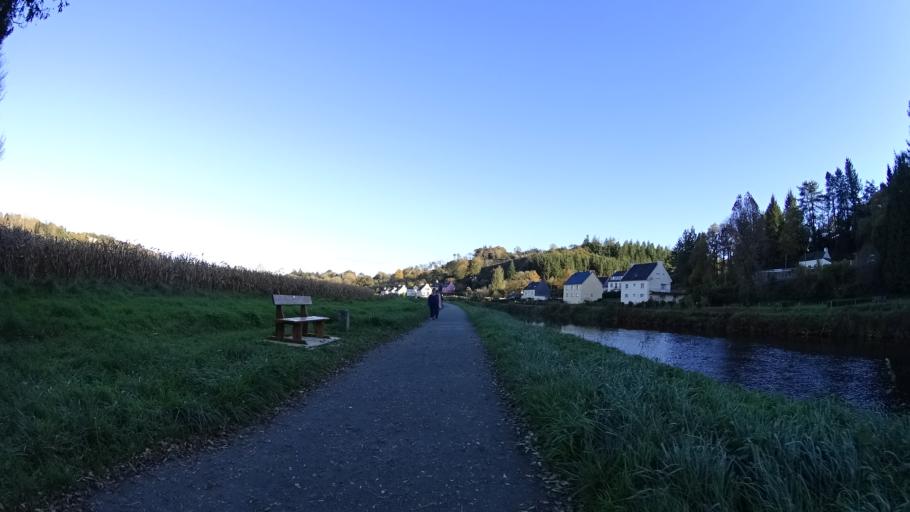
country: FR
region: Brittany
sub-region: Departement du Finistere
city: Chateaulin
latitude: 48.1883
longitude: -4.0883
